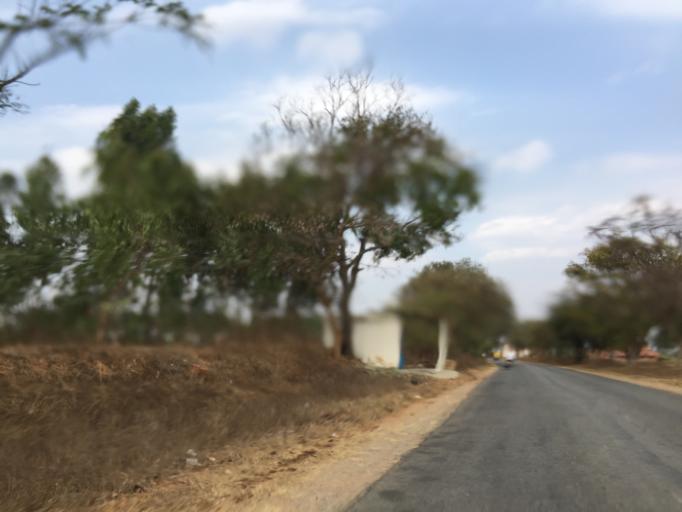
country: IN
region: Karnataka
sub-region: Chikkaballapur
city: Chik Ballapur
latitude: 13.4094
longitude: 77.7146
